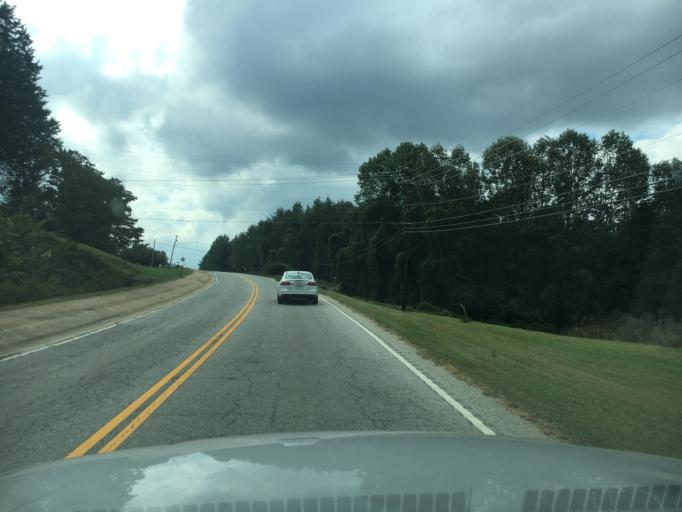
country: US
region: South Carolina
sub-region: Spartanburg County
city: Landrum
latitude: 35.1702
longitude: -82.1954
